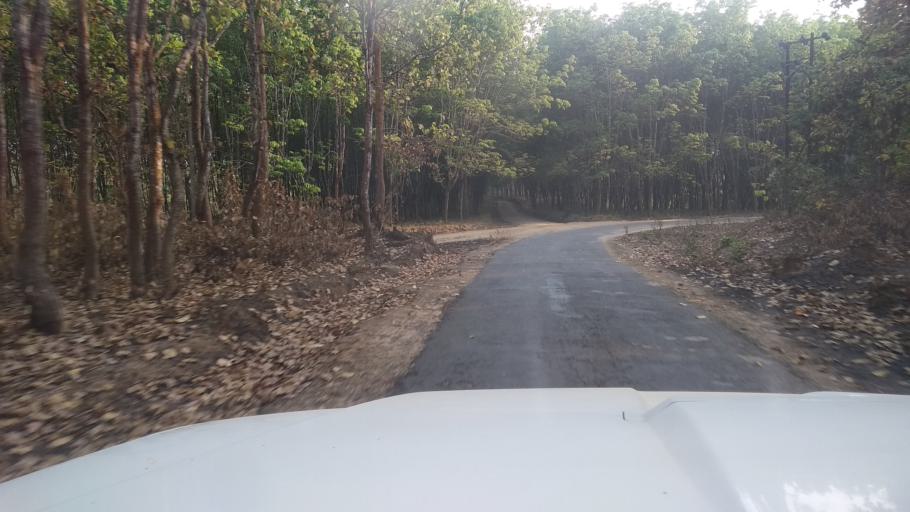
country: IN
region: Tripura
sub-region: West Tripura
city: Sonamura
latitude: 23.3304
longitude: 91.3092
